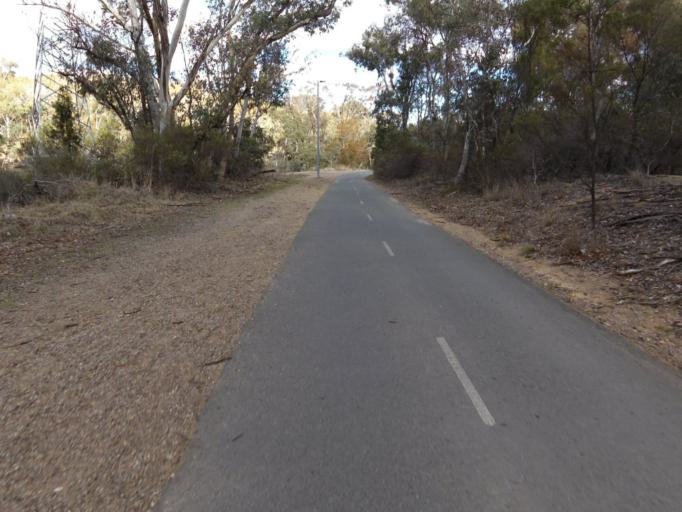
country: AU
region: Australian Capital Territory
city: Acton
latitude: -35.2520
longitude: 149.1075
